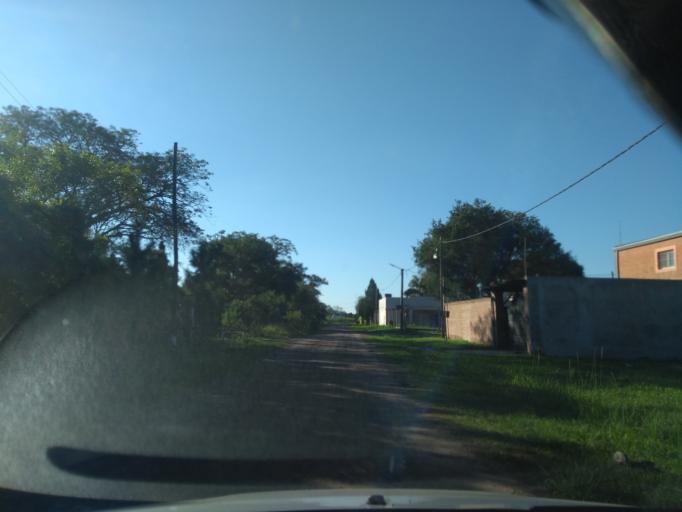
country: AR
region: Chaco
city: Barranqueras
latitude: -27.4386
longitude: -58.9099
